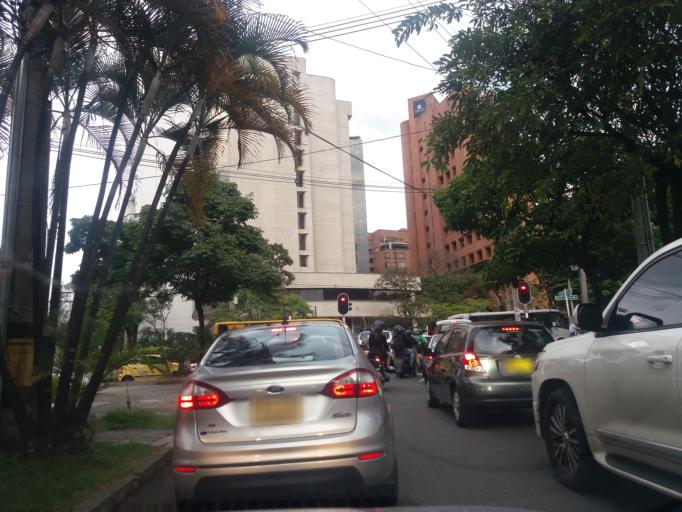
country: CO
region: Antioquia
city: Itagui
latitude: 6.2061
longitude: -75.5719
